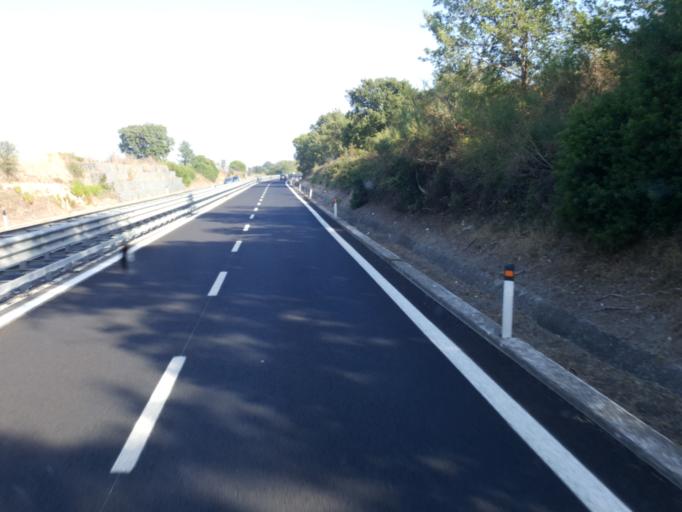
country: IT
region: Latium
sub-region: Provincia di Viterbo
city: Montalto di Castro
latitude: 42.3062
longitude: 11.6611
